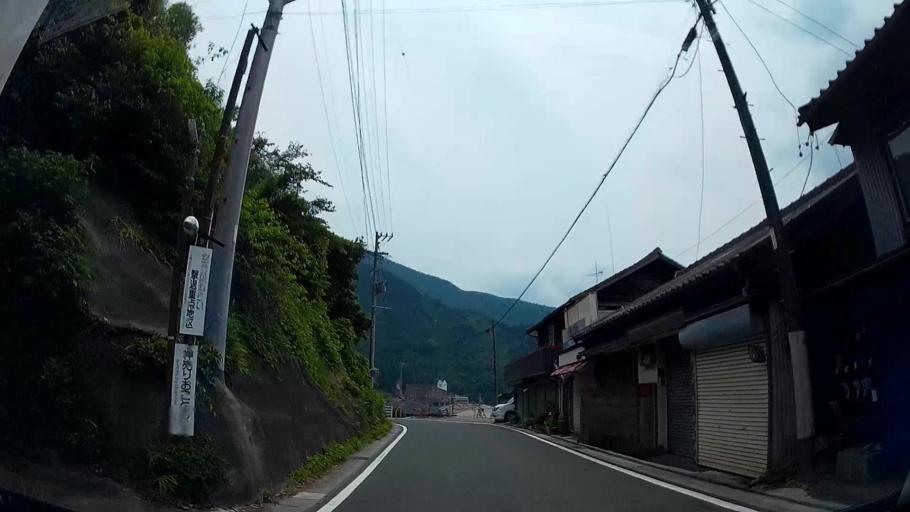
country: JP
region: Shizuoka
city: Mori
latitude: 35.0923
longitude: 137.8079
